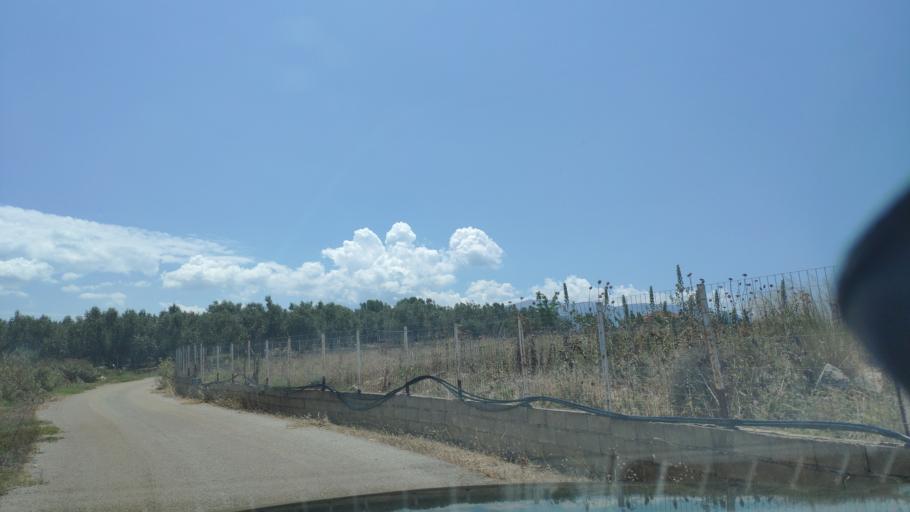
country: GR
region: West Greece
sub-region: Nomos Aitolias kai Akarnanias
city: Amfilochia
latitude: 38.9067
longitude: 21.1001
